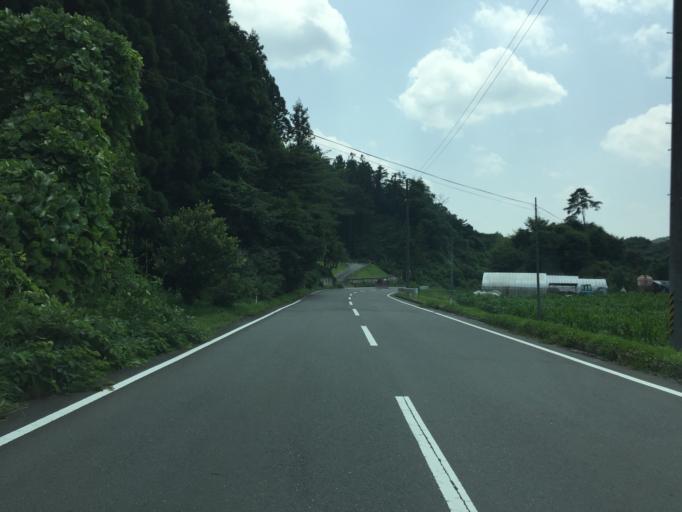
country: JP
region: Fukushima
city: Ishikawa
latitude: 37.2292
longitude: 140.5591
